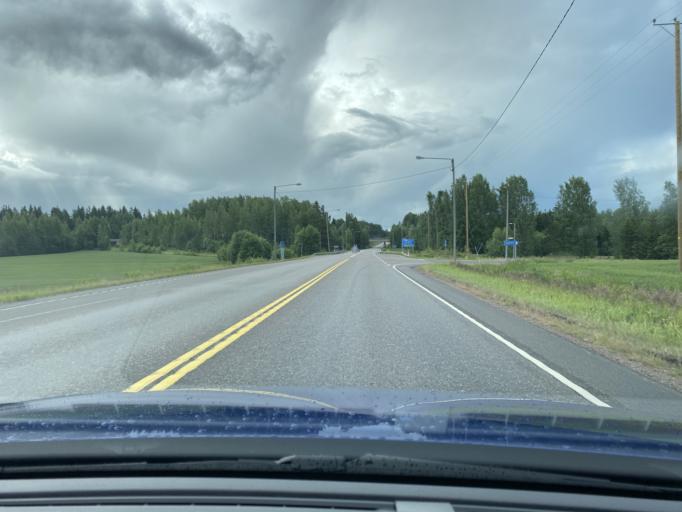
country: FI
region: Uusimaa
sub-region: Helsinki
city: Hyvinge
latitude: 60.5666
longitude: 24.8107
